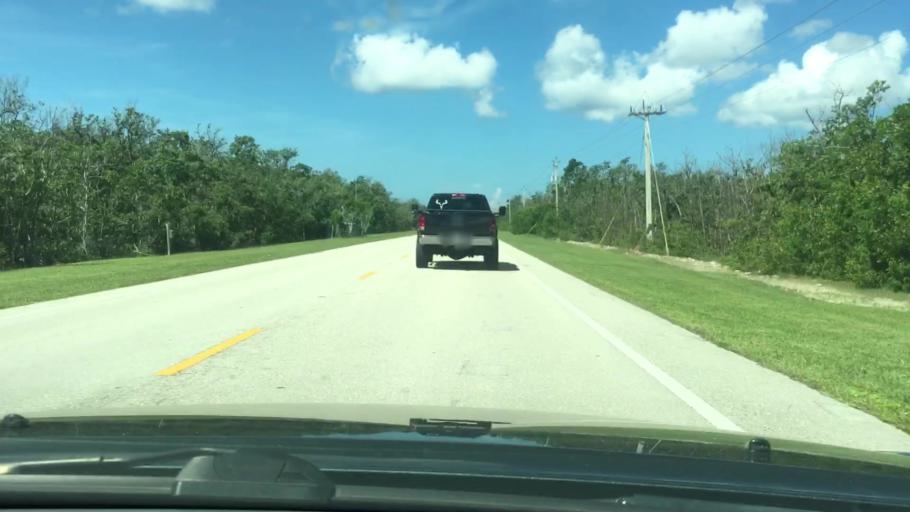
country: US
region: Florida
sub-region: Collier County
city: Marco
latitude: 25.9320
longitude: -81.6668
